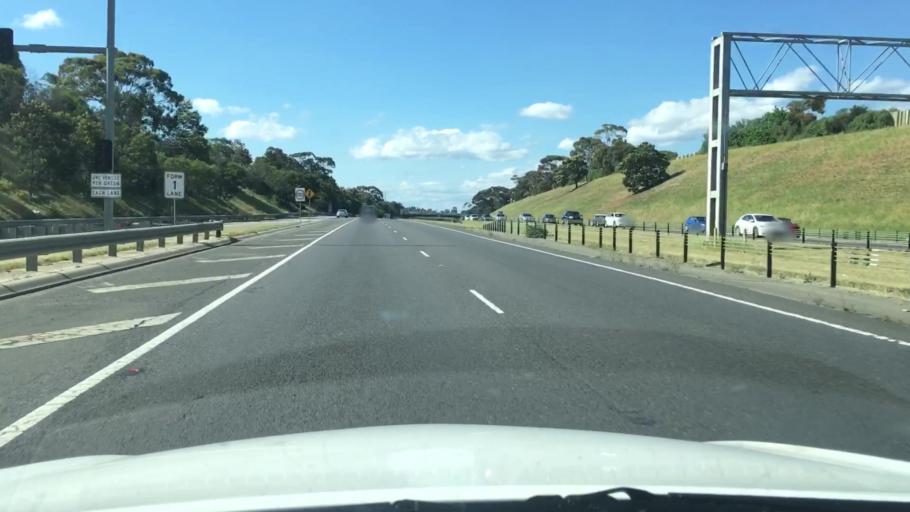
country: AU
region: Victoria
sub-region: Casey
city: Eumemmerring
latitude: -38.0016
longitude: 145.2520
